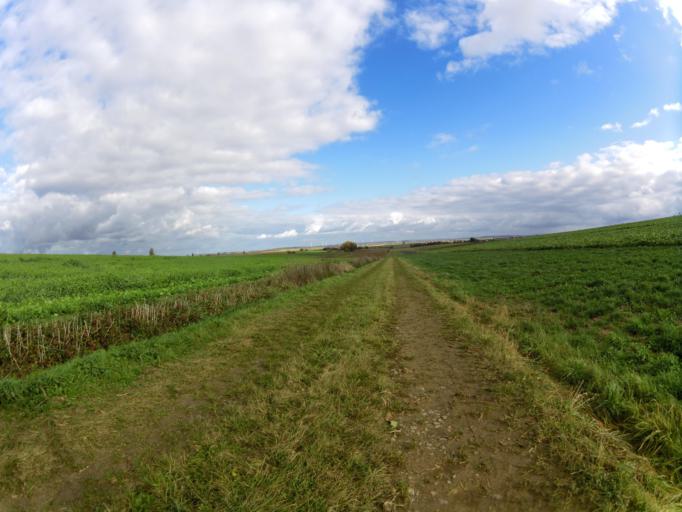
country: DE
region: Bavaria
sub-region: Regierungsbezirk Unterfranken
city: Unterpleichfeld
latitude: 49.8793
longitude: 10.0085
